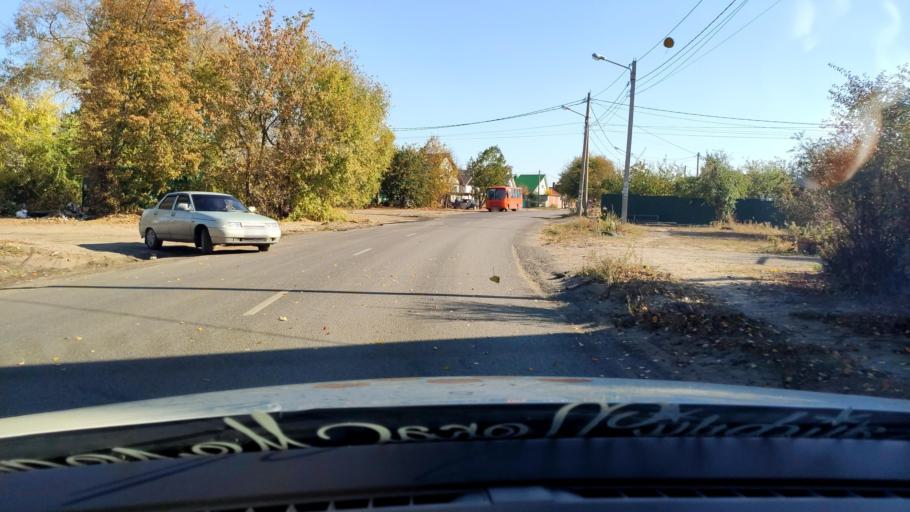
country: RU
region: Voronezj
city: Pridonskoy
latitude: 51.6835
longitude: 39.0692
